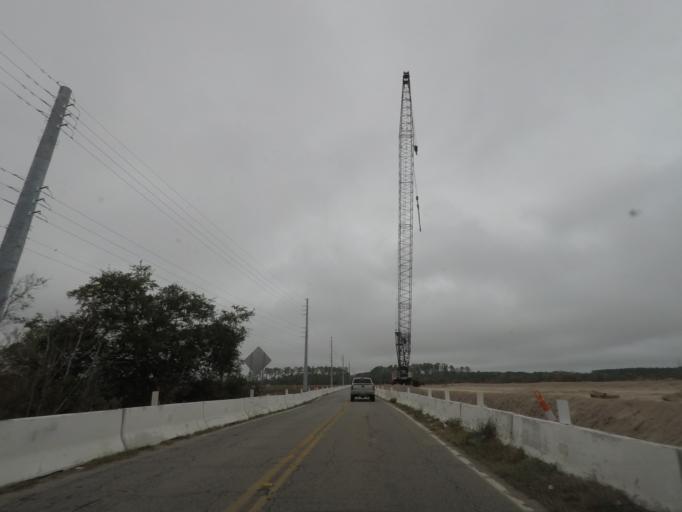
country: US
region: South Carolina
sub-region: Charleston County
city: Meggett
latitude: 32.6136
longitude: -80.3446
